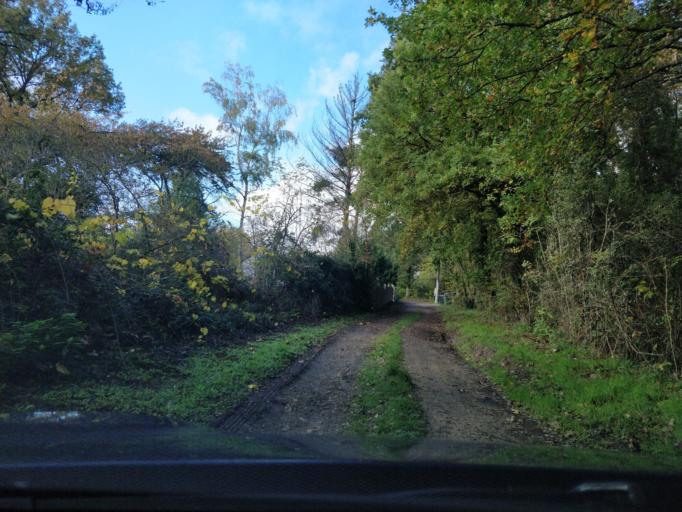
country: FR
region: Ile-de-France
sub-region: Departement de l'Essonne
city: Briis-sous-Forges
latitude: 48.6252
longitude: 2.1354
